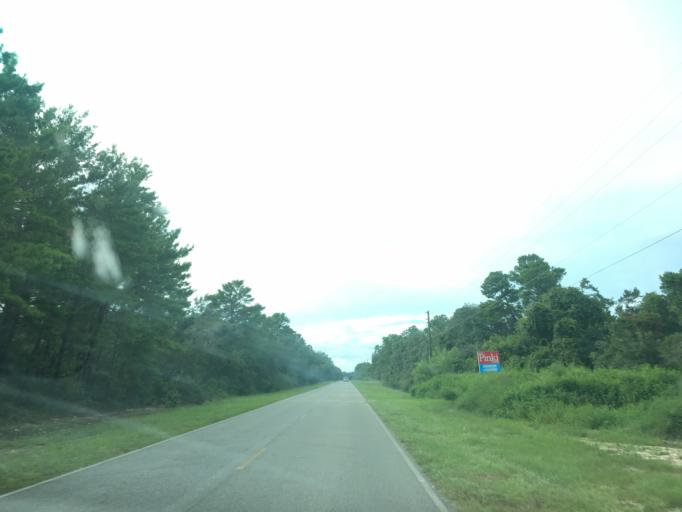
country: US
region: Florida
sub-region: Wakulla County
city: Crawfordville
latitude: 29.9182
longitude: -84.3703
